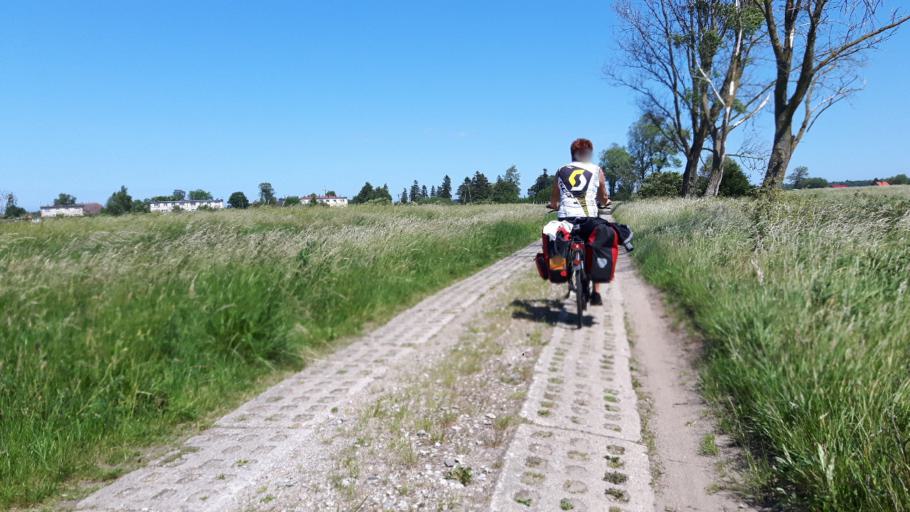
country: PL
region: Pomeranian Voivodeship
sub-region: Powiat slupski
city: Smoldzino
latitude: 54.6837
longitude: 17.2787
